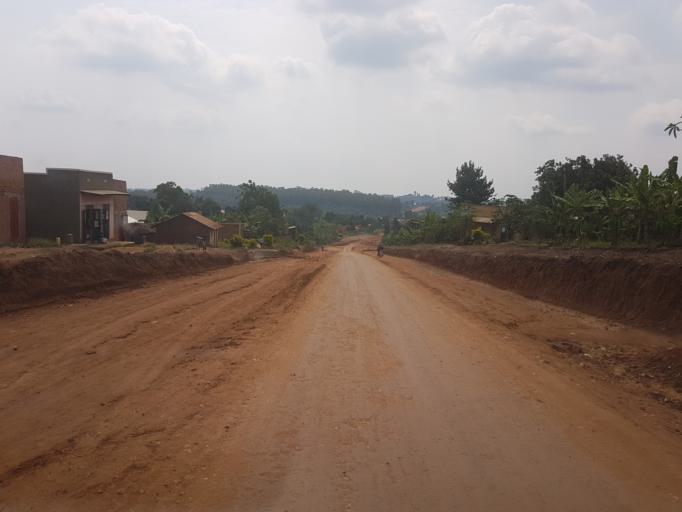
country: UG
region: Western Region
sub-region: Kanungu District
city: Ntungamo
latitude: -0.8060
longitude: 29.7044
